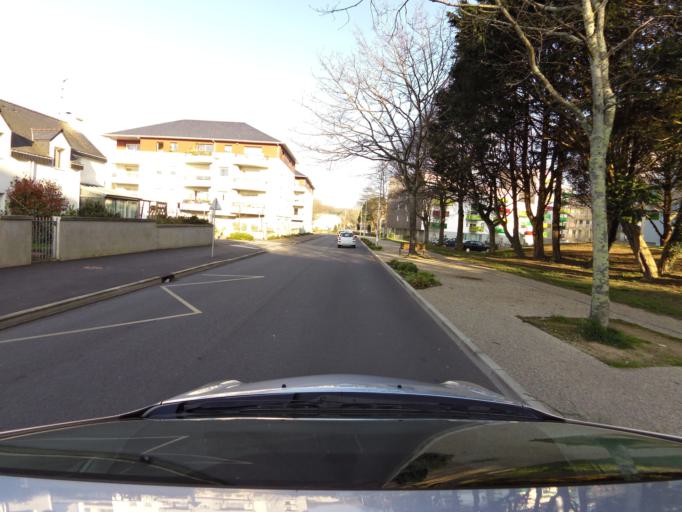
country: FR
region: Brittany
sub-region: Departement du Morbihan
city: Lorient
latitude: 47.7388
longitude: -3.3920
